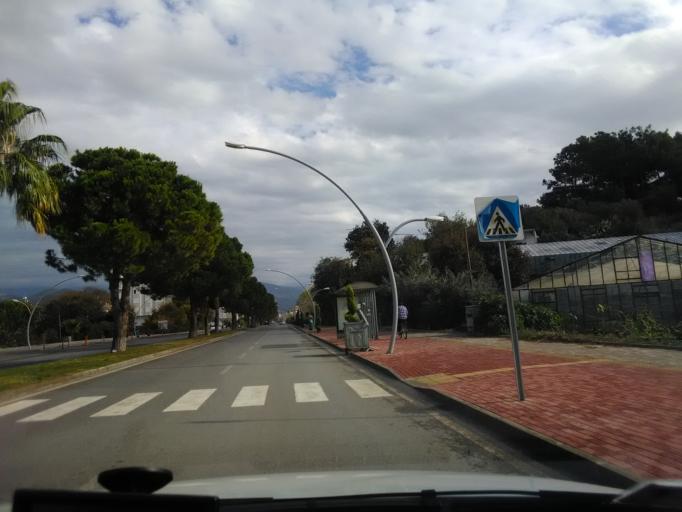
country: TR
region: Antalya
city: Gazipasa
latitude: 36.2652
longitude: 32.2911
